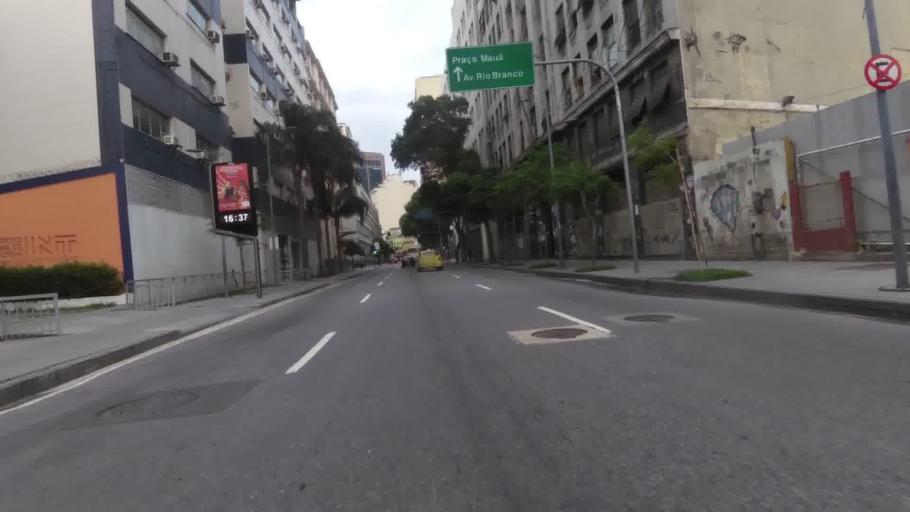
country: BR
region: Rio de Janeiro
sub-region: Rio De Janeiro
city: Rio de Janeiro
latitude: -22.8963
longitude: -43.1849
